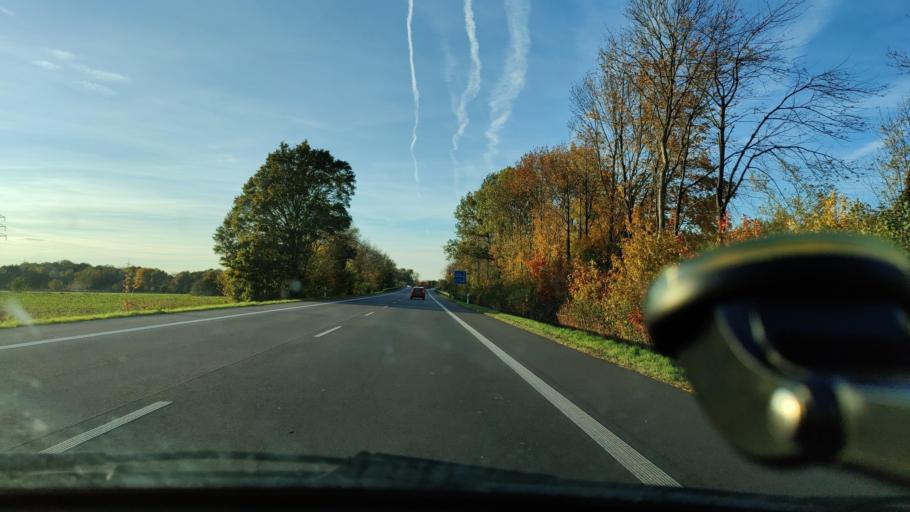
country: DE
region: North Rhine-Westphalia
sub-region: Regierungsbezirk Dusseldorf
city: Monchengladbach
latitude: 51.2314
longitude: 6.4601
